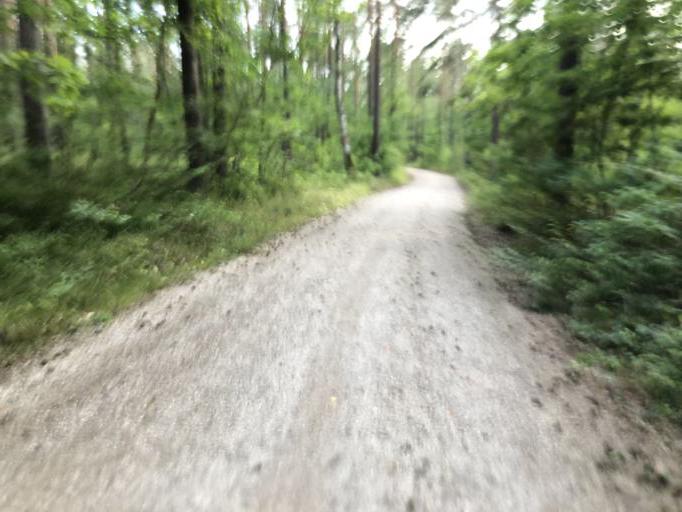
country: DE
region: Bavaria
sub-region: Regierungsbezirk Mittelfranken
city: Buckenhof
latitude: 49.5869
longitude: 11.0625
